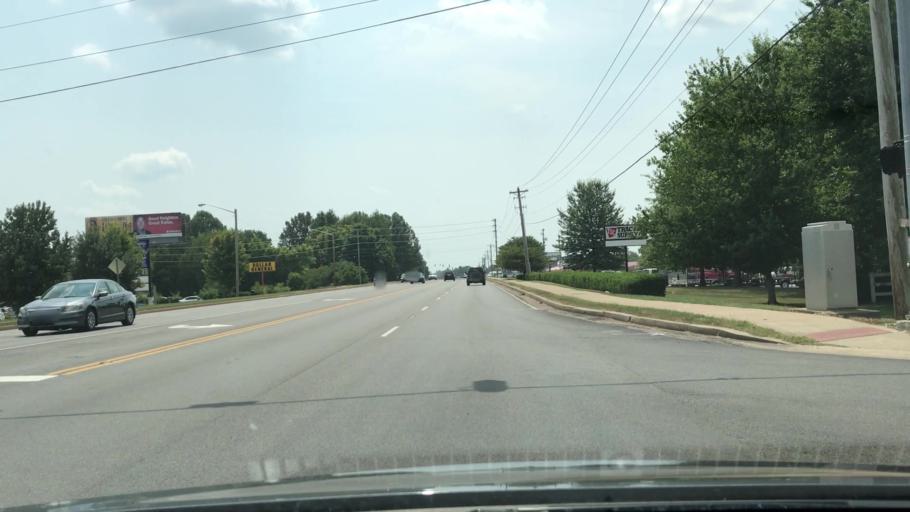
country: US
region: Kentucky
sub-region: Warren County
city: Plano
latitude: 36.9236
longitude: -86.4104
